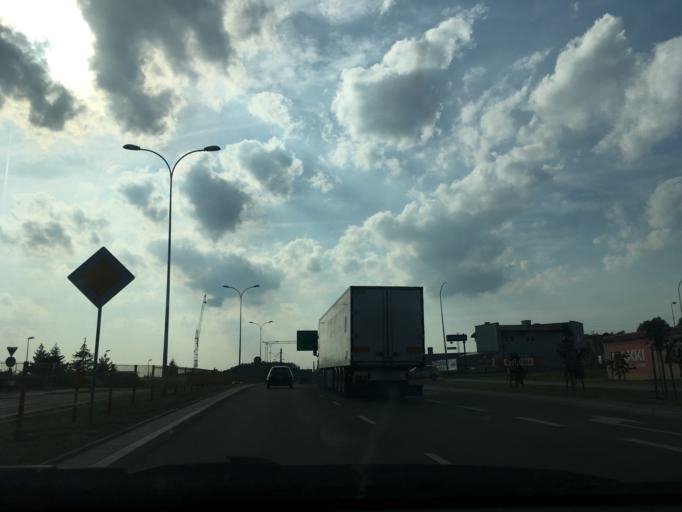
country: PL
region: Podlasie
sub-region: Bialystok
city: Bialystok
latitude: 53.1391
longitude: 23.2092
